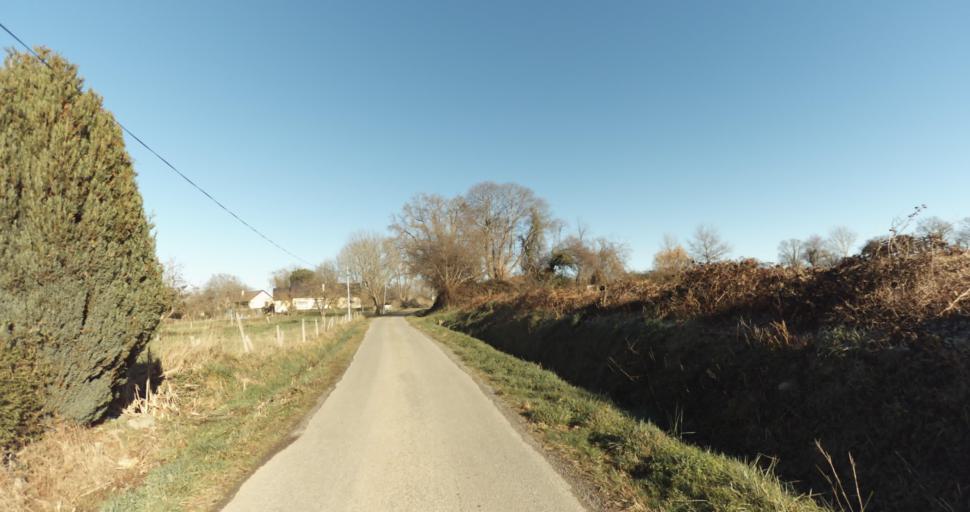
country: FR
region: Aquitaine
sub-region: Departement des Pyrenees-Atlantiques
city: Morlaas
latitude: 43.3421
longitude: -0.2442
